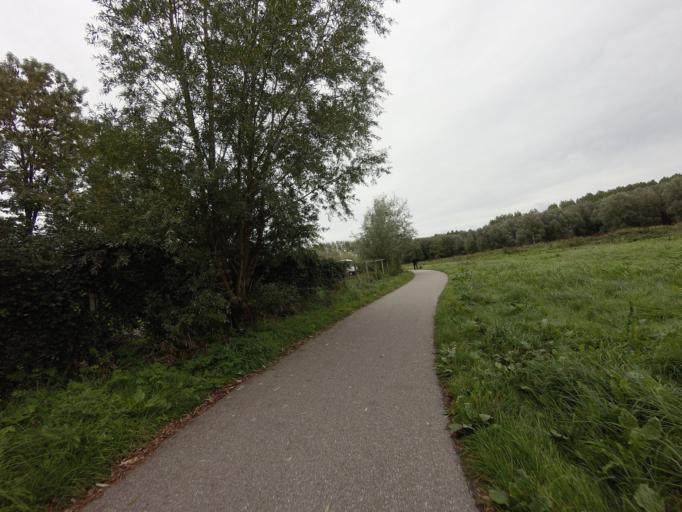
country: NL
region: Friesland
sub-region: Gemeente Leeuwarden
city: Bilgaard
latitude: 53.2188
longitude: 5.7926
